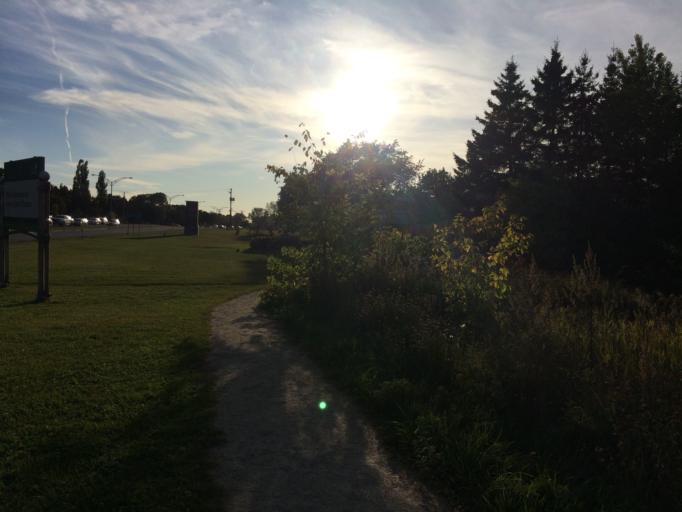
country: CA
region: Quebec
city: Quebec
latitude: 46.8081
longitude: -71.2693
